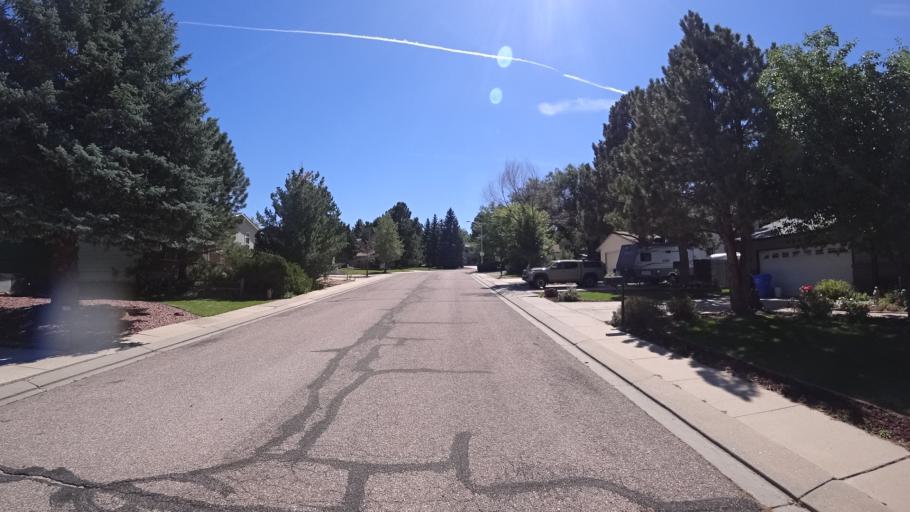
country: US
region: Colorado
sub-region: El Paso County
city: Colorado Springs
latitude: 38.9236
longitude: -104.7983
